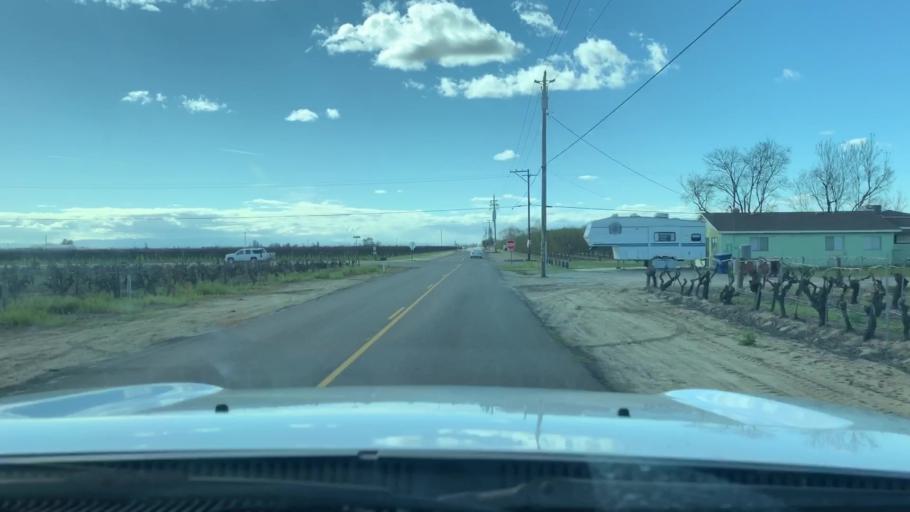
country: US
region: California
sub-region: Fresno County
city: Caruthers
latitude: 36.5619
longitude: -119.7541
